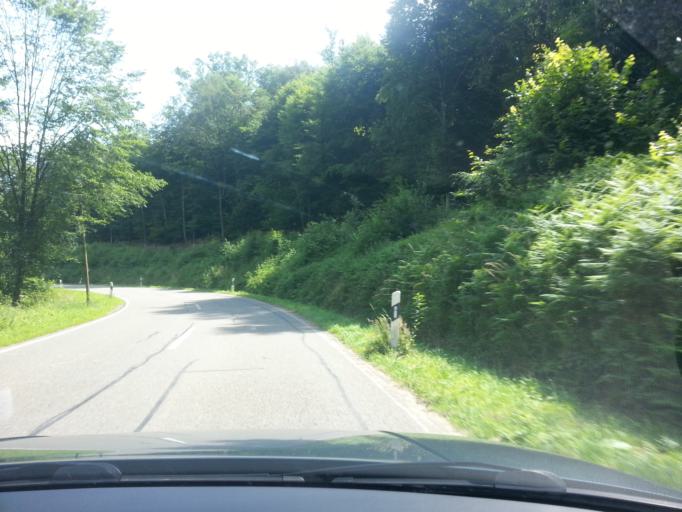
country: DE
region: Saarland
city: Spiesen-Elversberg
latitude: 49.3038
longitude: 7.1555
